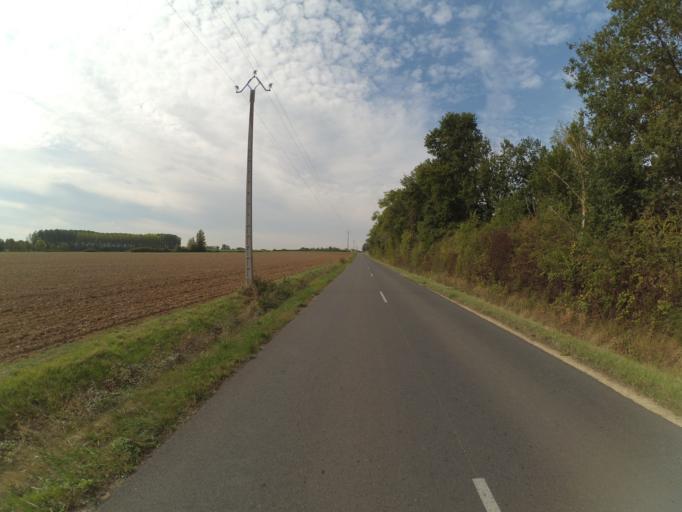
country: FR
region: Pays de la Loire
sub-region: Departement de Maine-et-Loire
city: Martigne-Briand
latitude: 47.2014
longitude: -0.4154
